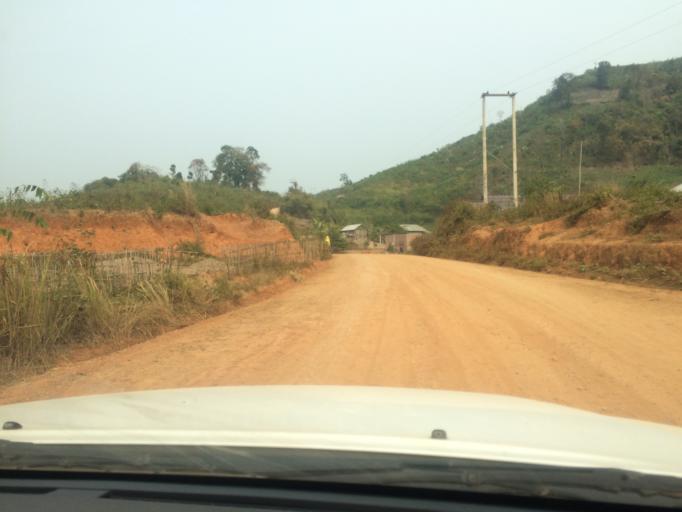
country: LA
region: Loungnamtha
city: Muang Nale
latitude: 20.4346
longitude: 101.7106
